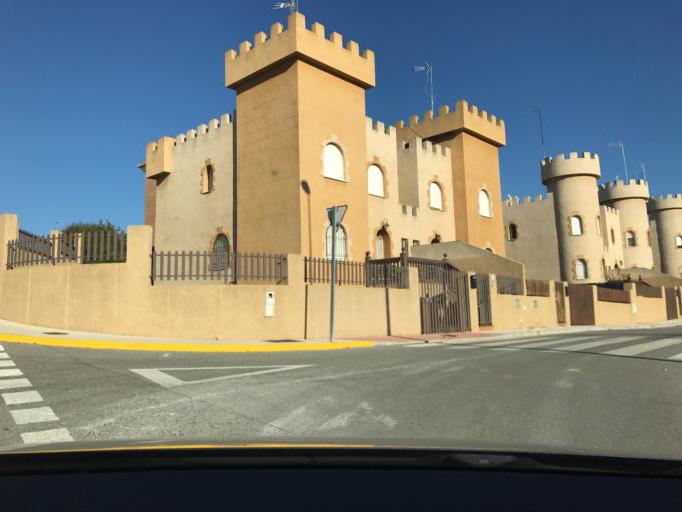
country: ES
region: Andalusia
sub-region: Provincia de Granada
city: Peligros
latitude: 37.2358
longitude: -3.6160
